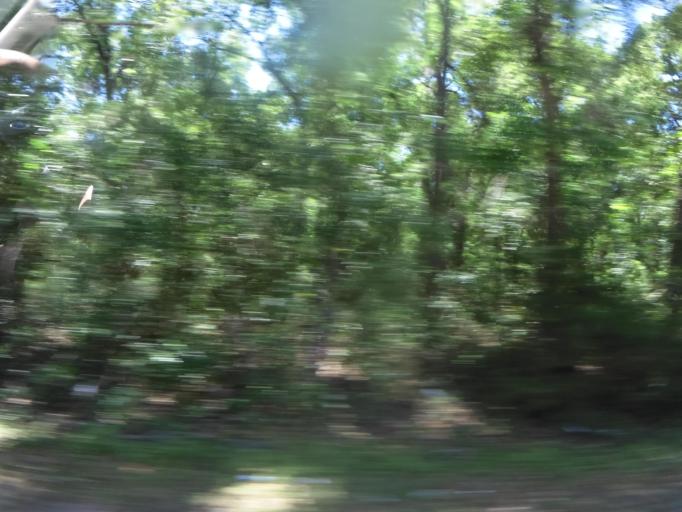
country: US
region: Florida
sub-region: Duval County
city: Atlantic Beach
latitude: 30.4578
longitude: -81.5195
